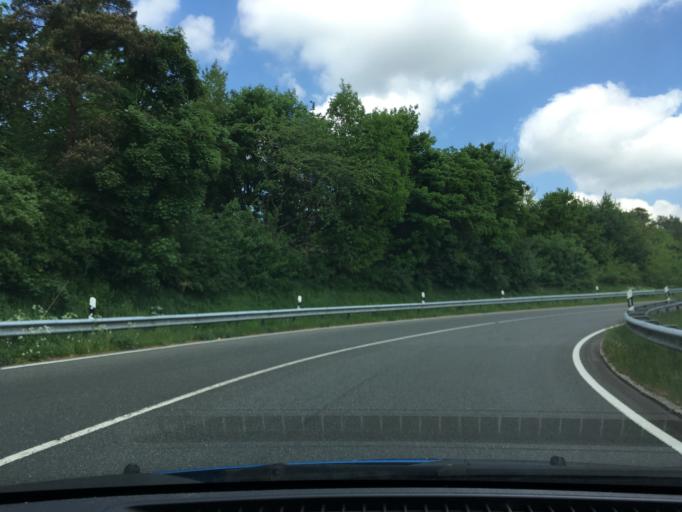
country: DE
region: Lower Saxony
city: Deutsch Evern
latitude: 53.2133
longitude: 10.4399
